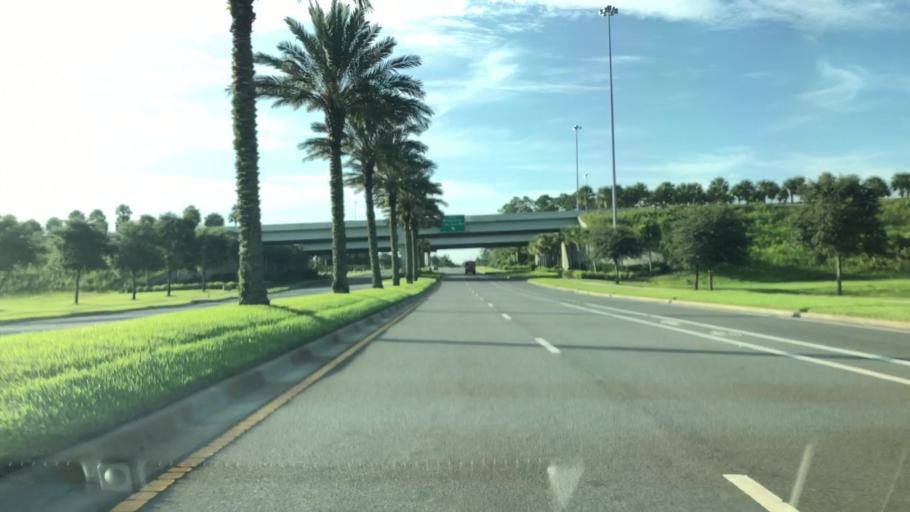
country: US
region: Florida
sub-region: Saint Johns County
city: Palm Valley
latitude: 30.1121
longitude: -81.4475
